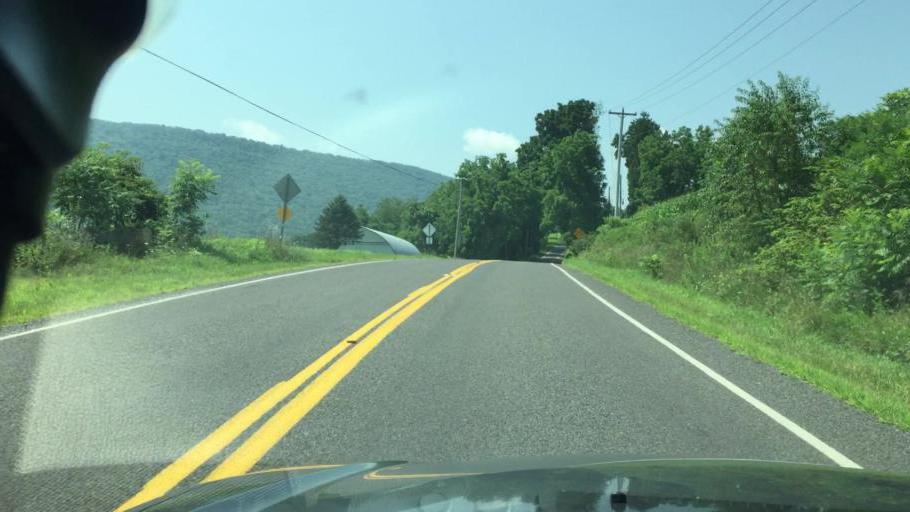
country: US
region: Pennsylvania
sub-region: Columbia County
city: Mifflinville
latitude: 40.9992
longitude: -76.3249
